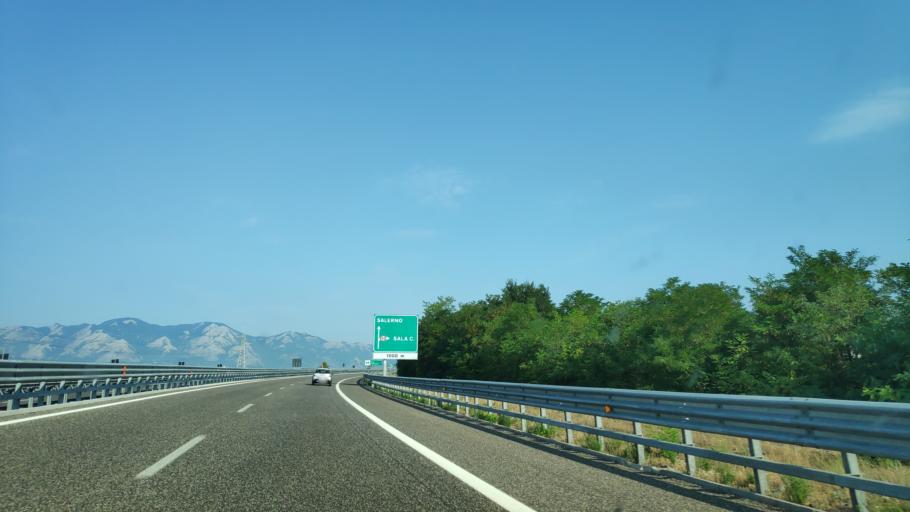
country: IT
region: Campania
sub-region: Provincia di Salerno
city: Sala Consilina
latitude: 40.4094
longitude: 15.5662
